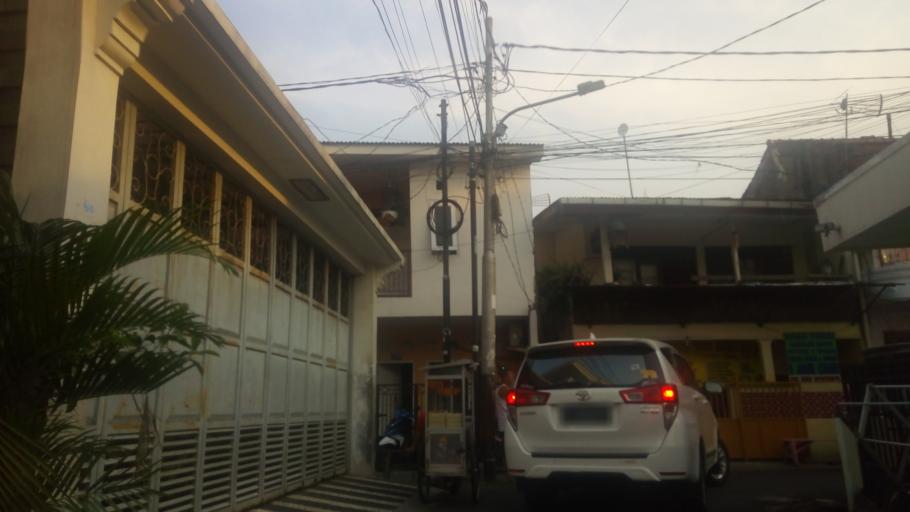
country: ID
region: Jakarta Raya
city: Jakarta
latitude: -6.2056
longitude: 106.8539
